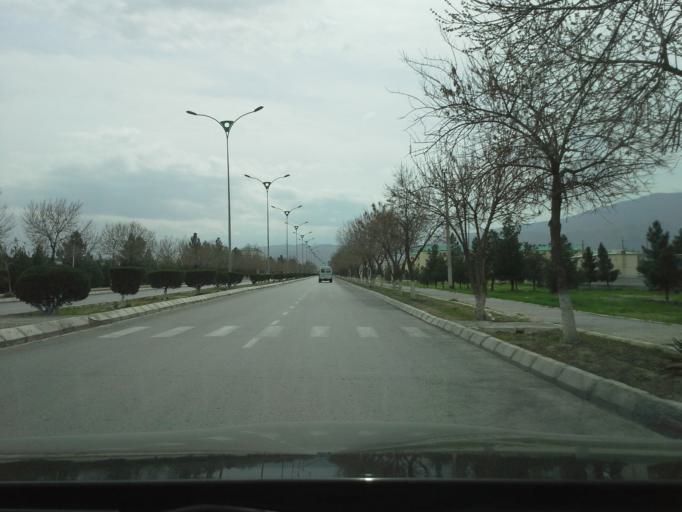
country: TM
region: Ahal
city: Abadan
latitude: 38.0600
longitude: 58.1587
